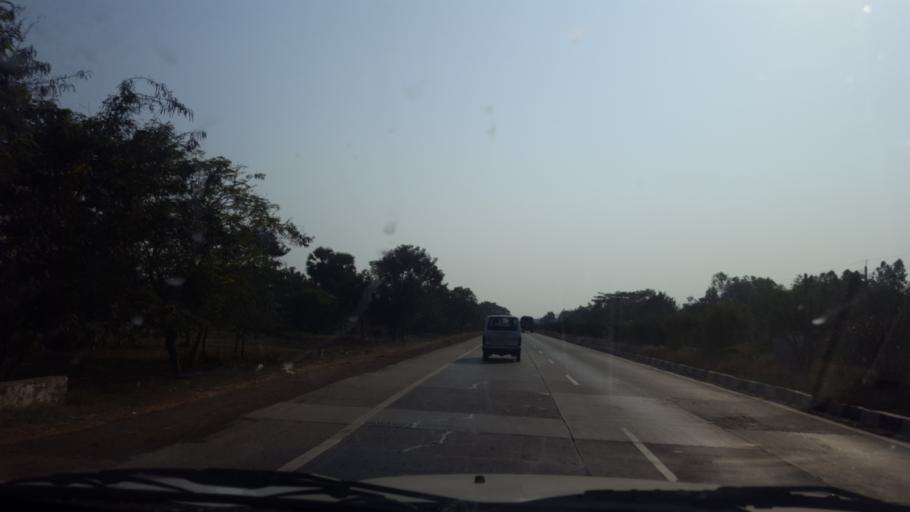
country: IN
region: Andhra Pradesh
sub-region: Vishakhapatnam
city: Elamanchili
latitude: 17.5483
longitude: 82.8395
